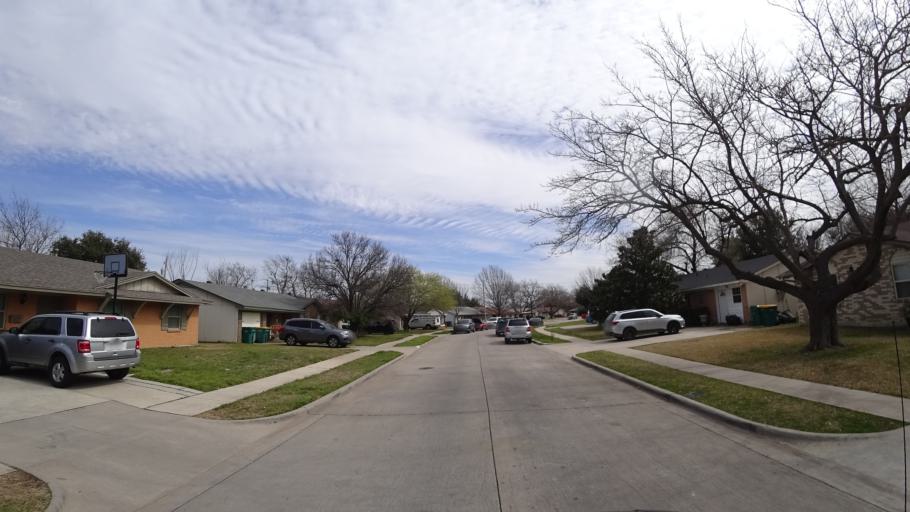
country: US
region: Texas
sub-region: Denton County
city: Lewisville
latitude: 33.0387
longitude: -97.0125
